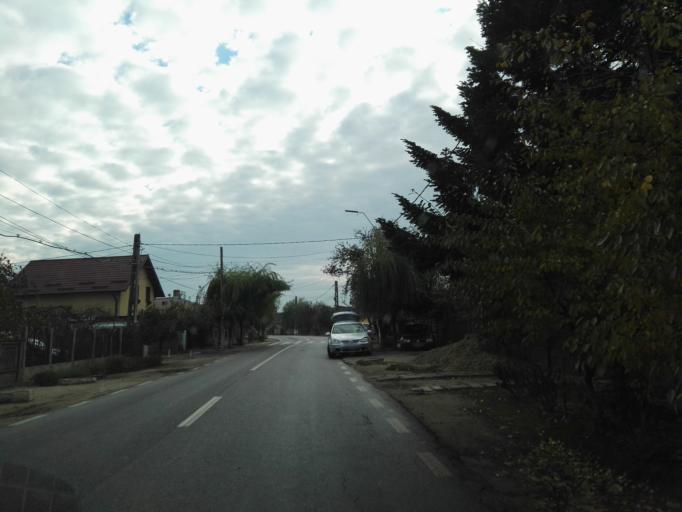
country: RO
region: Ilfov
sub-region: Comuna Magurele
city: Alunisu
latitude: 44.3423
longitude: 26.0452
